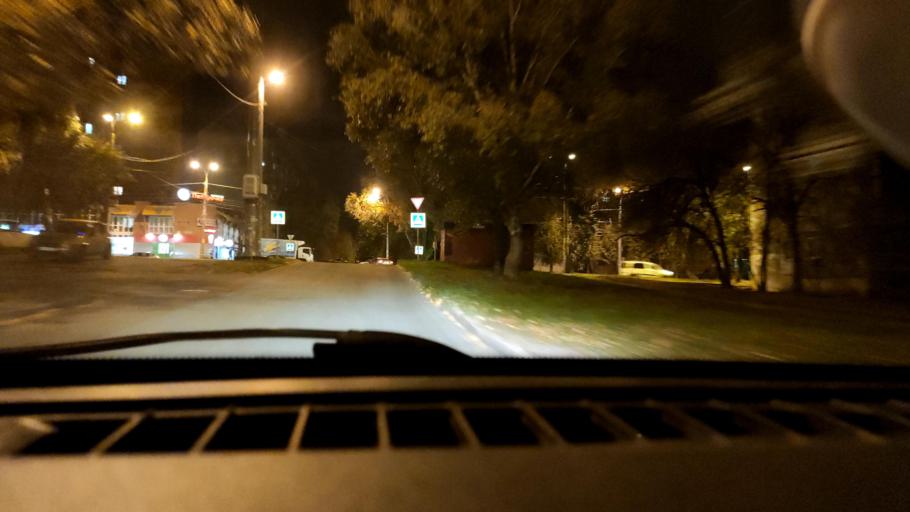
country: RU
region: Samara
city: Samara
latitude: 53.2185
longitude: 50.2267
